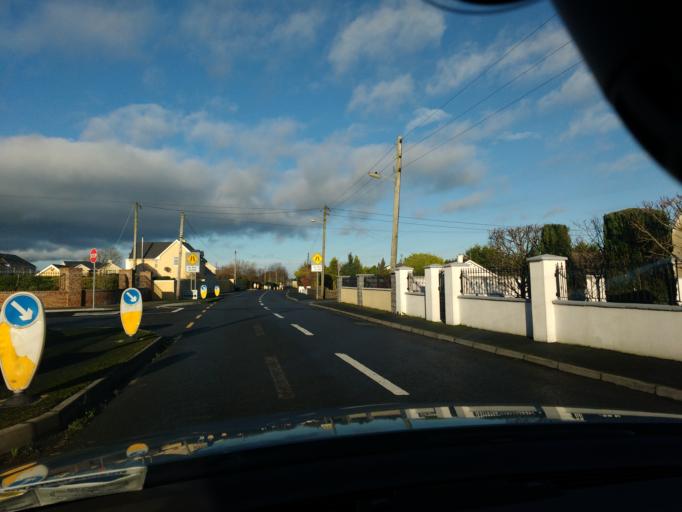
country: IE
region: Leinster
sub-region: Laois
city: Rathdowney
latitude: 52.7164
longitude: -7.5843
